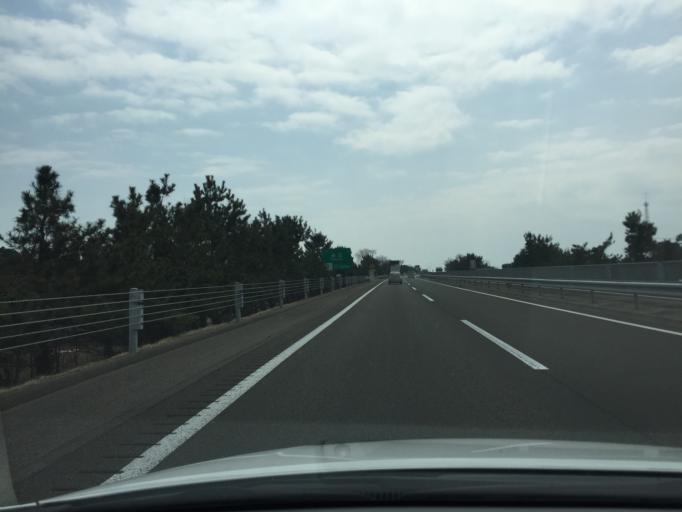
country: JP
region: Miyagi
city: Iwanuma
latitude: 38.1138
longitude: 140.8885
